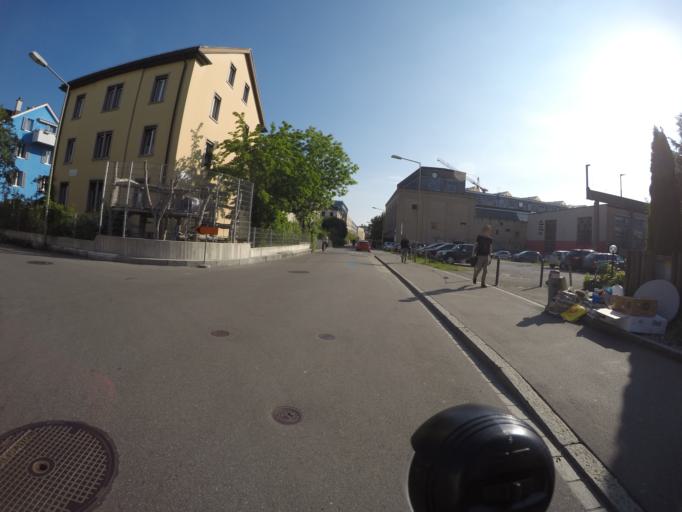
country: CH
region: Zurich
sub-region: Bezirk Winterthur
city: Stadt Winterthur (Kreis 1) / Toessfeld
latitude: 47.4929
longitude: 8.7152
